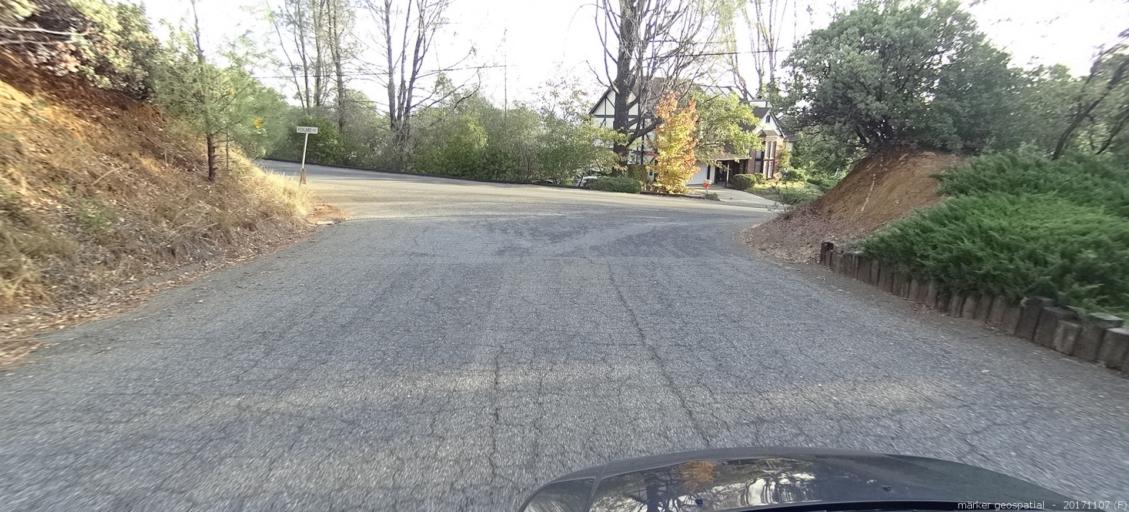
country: US
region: California
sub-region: Shasta County
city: Shasta
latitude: 40.5866
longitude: -122.4696
